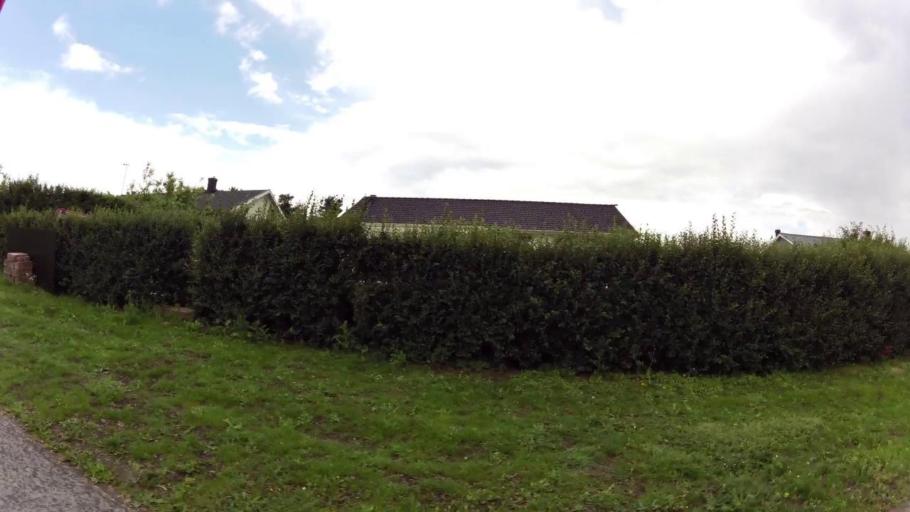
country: SE
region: OEstergoetland
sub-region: Linkopings Kommun
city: Sturefors
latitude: 58.3850
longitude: 15.7045
